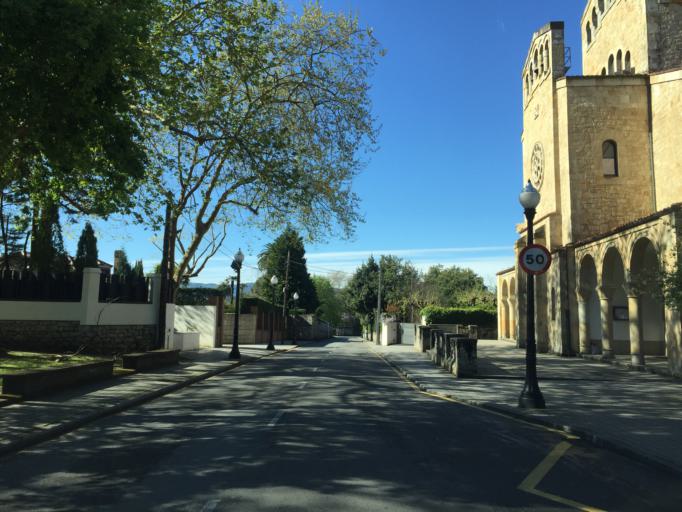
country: ES
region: Asturias
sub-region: Province of Asturias
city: Gijon
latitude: 43.5356
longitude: -5.6231
